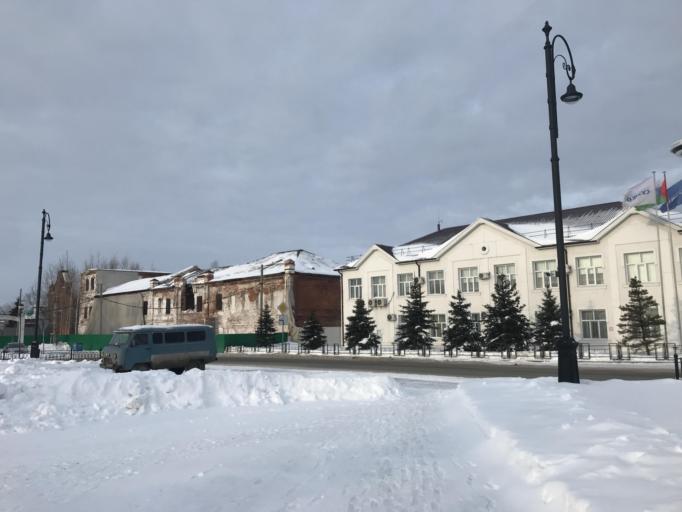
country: RU
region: Tjumen
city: Tobol'sk
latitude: 58.1975
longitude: 68.2443
